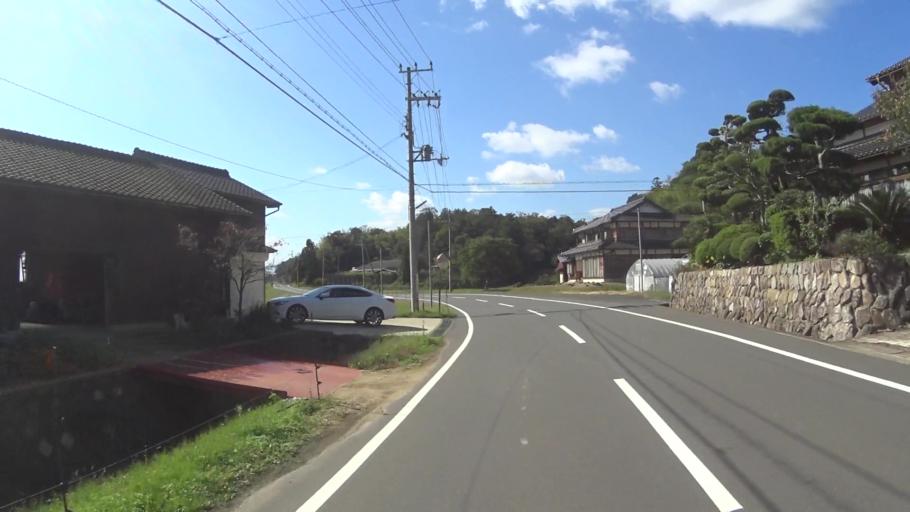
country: JP
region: Kyoto
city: Miyazu
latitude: 35.6954
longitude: 135.0990
